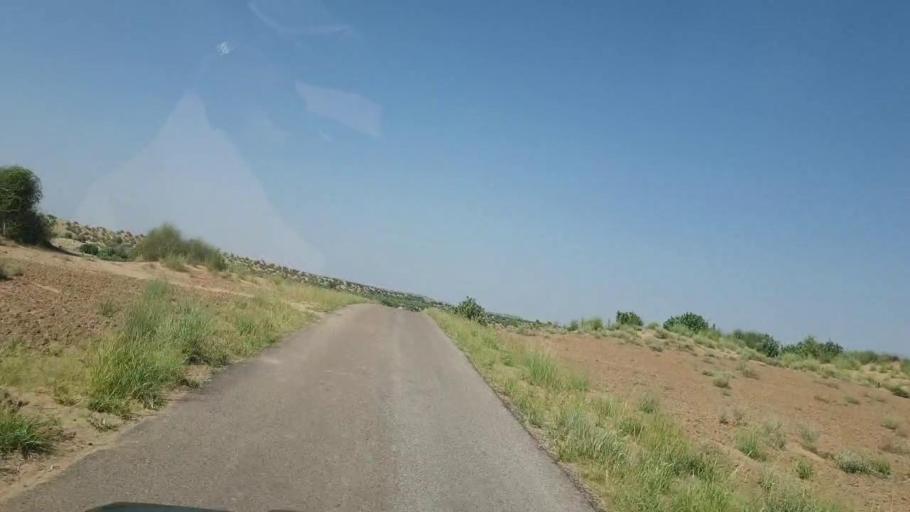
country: PK
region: Sindh
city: Chor
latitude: 25.6339
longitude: 70.3175
